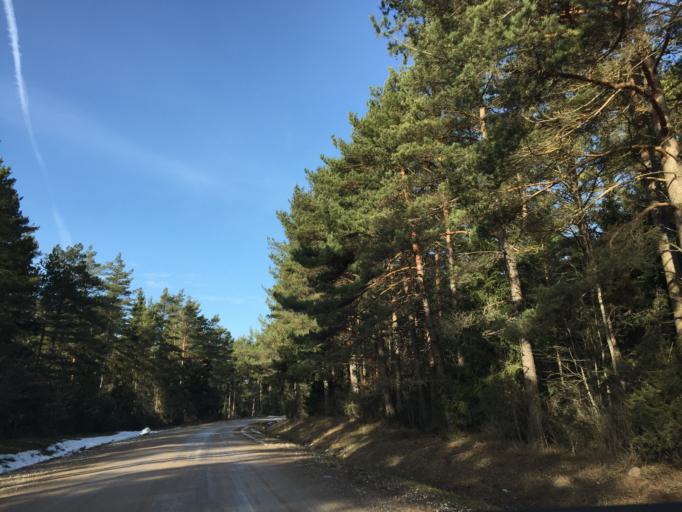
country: EE
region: Saare
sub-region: Kuressaare linn
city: Kuressaare
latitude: 58.3713
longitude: 22.0163
